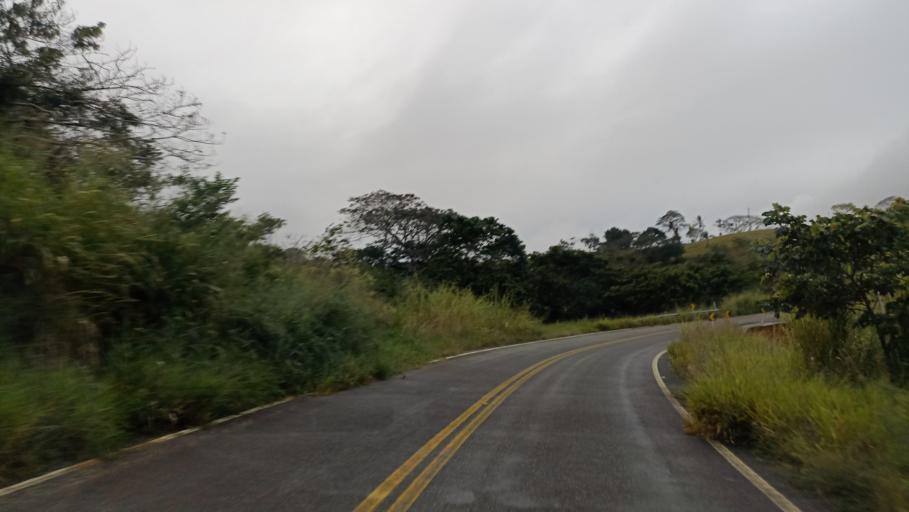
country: BR
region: Minas Gerais
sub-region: Joaima
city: Joaima
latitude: -16.6733
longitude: -40.5278
